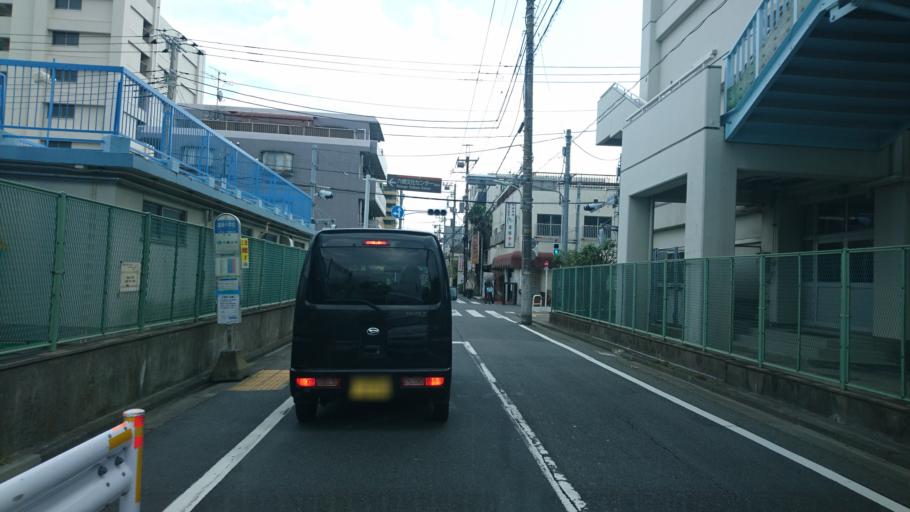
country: JP
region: Kanagawa
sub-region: Kawasaki-shi
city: Kawasaki
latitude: 35.5451
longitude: 139.7070
